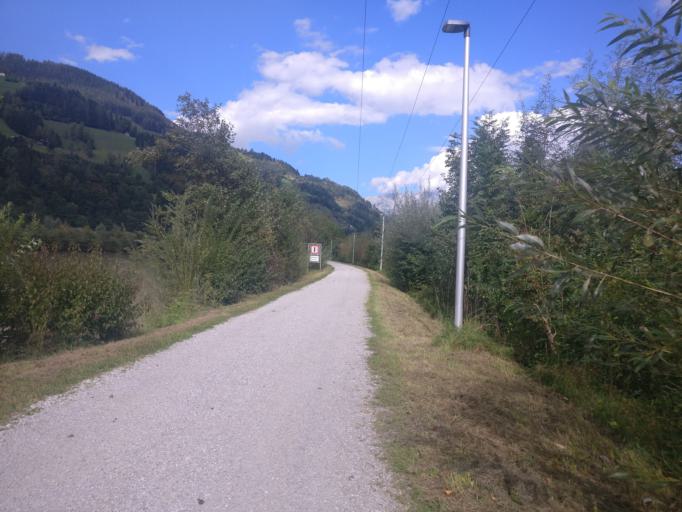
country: AT
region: Salzburg
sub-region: Politischer Bezirk Sankt Johann im Pongau
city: Sankt Johann im Pongau
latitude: 47.3697
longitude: 13.2105
